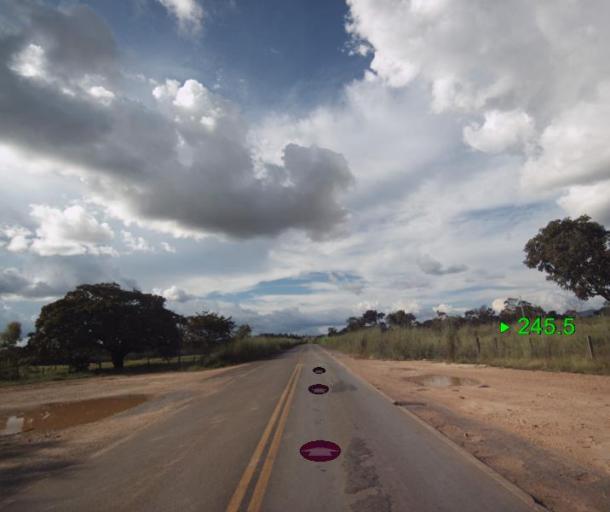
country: BR
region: Goias
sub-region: Barro Alto
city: Barro Alto
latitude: -14.7877
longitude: -48.6311
